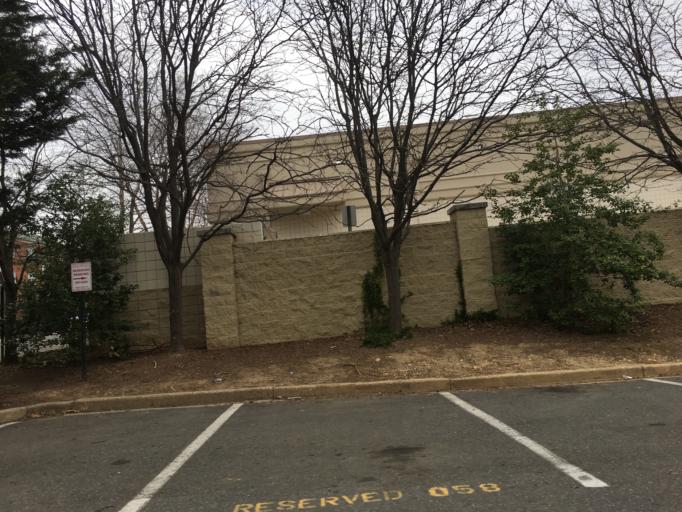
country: US
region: Virginia
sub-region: Fairfax County
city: Baileys Crossroads
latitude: 38.8554
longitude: -77.1413
